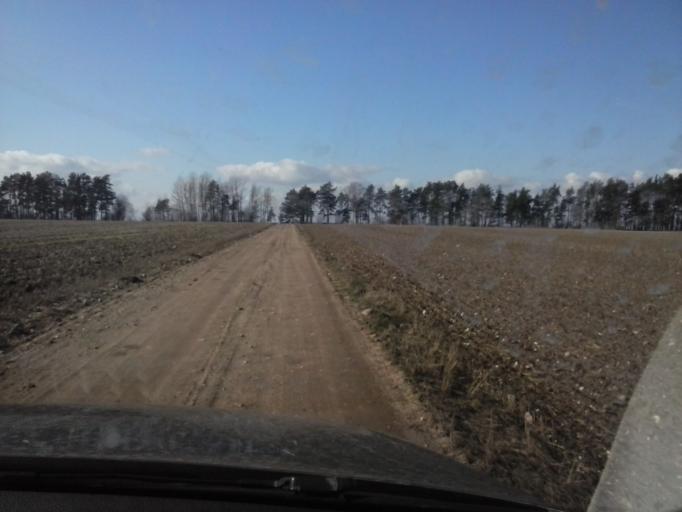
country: EE
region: Tartu
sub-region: Puhja vald
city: Puhja
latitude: 58.2848
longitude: 26.1456
